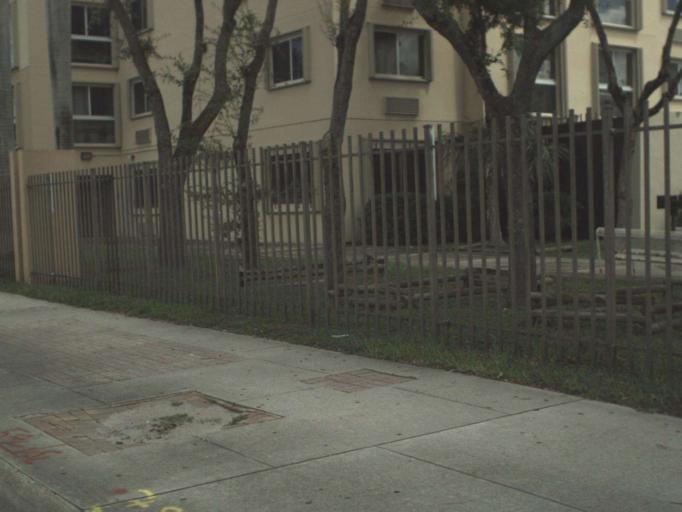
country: US
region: Florida
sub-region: Miami-Dade County
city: Allapattah
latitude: 25.8288
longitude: -80.2083
